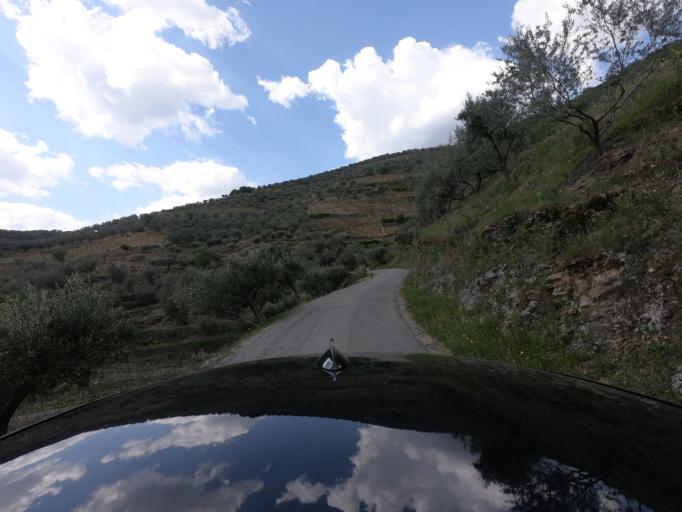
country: PT
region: Vila Real
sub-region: Sabrosa
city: Vilela
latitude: 41.2007
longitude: -7.6609
